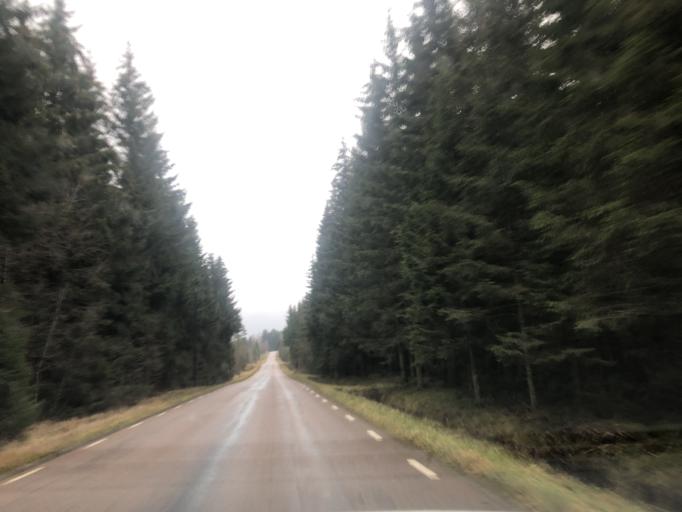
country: SE
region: Vaestra Goetaland
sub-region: Ulricehamns Kommun
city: Ulricehamn
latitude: 57.8271
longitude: 13.5092
